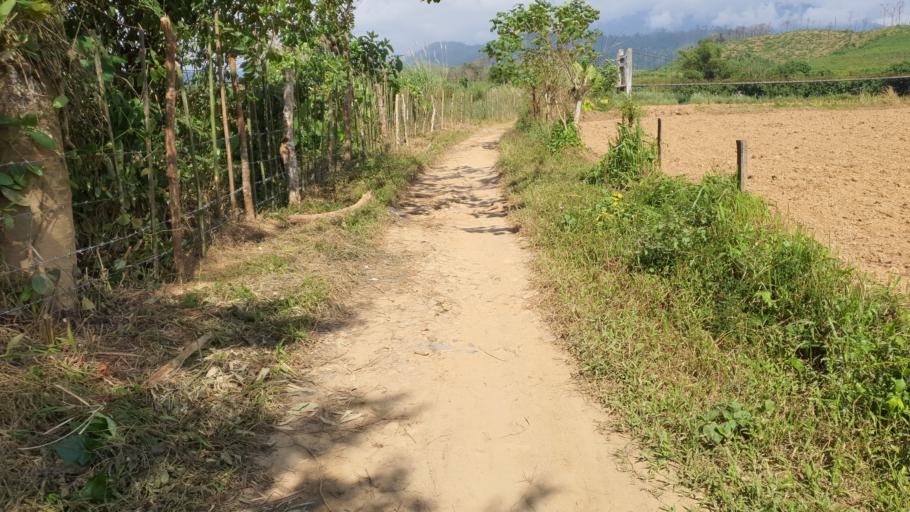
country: LA
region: Bolikhamxai
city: Bolikhan
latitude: 18.9079
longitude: 103.7427
